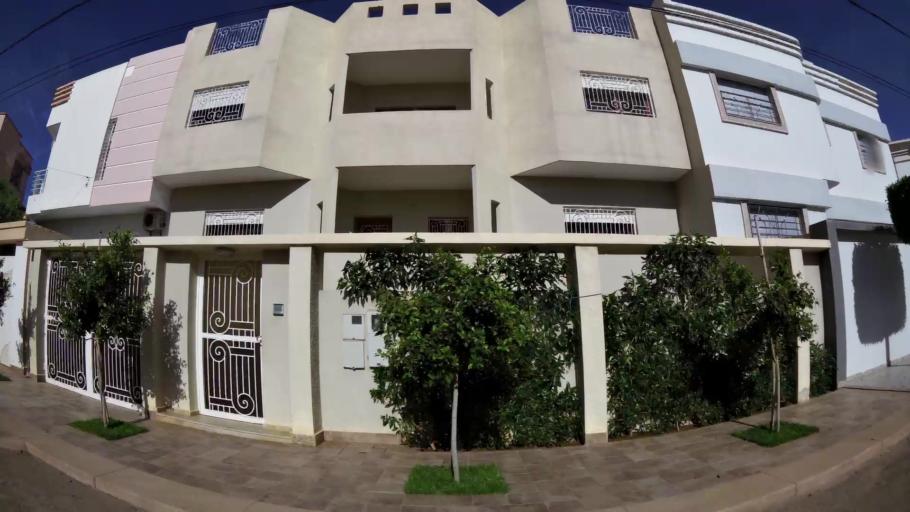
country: MA
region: Oriental
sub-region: Oujda-Angad
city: Oujda
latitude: 34.6658
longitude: -1.9002
